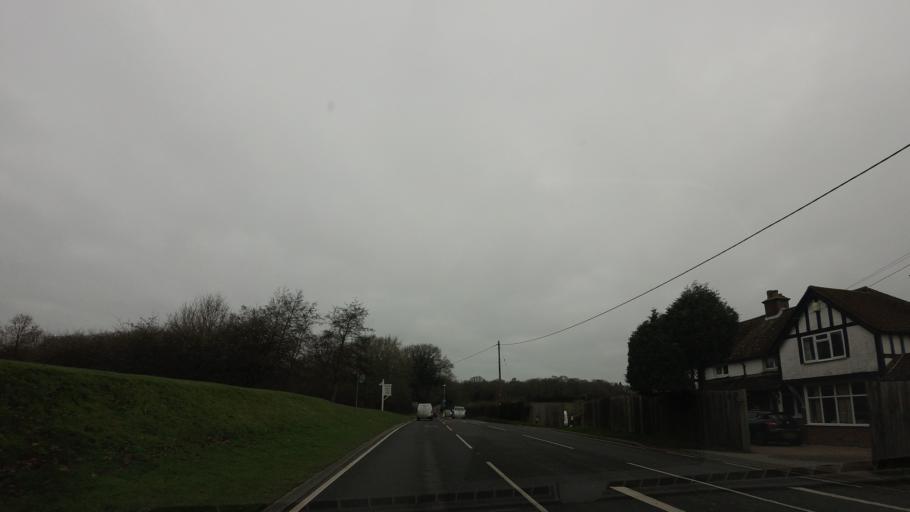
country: GB
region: England
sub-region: East Sussex
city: Battle
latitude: 50.9147
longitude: 0.5406
